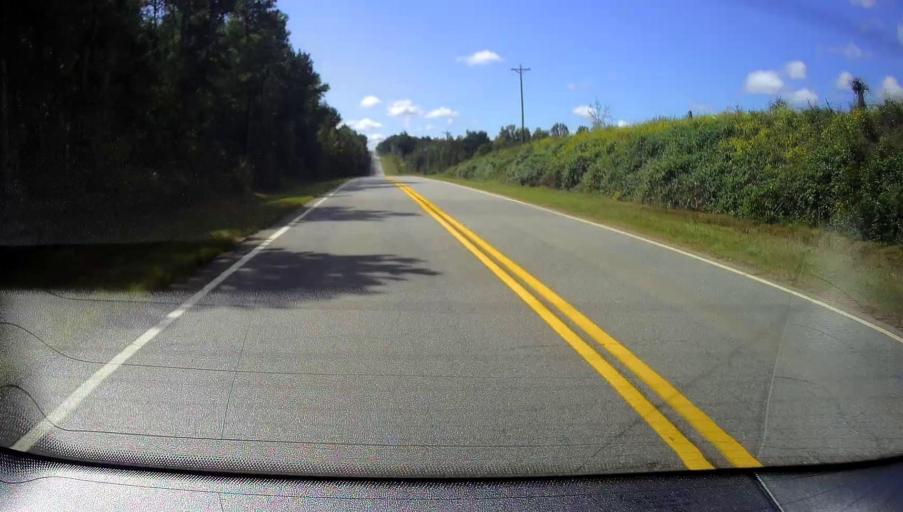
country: US
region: Georgia
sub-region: Jones County
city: Gray
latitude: 32.9584
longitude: -83.4421
